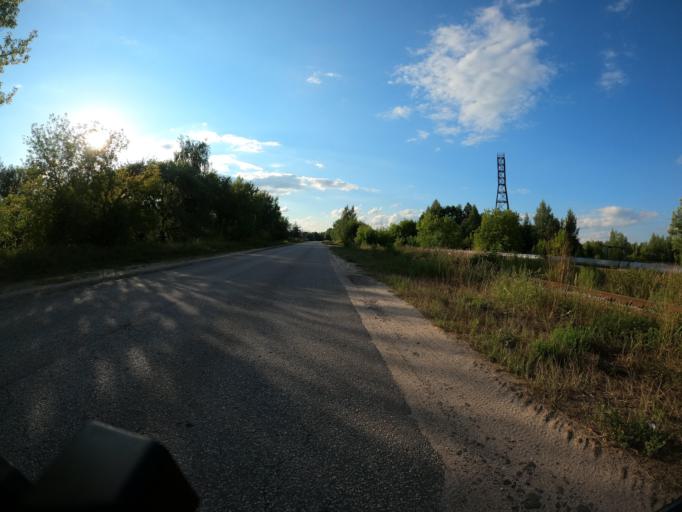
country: RU
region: Moskovskaya
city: Beloozerskiy
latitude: 55.4539
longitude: 38.4867
